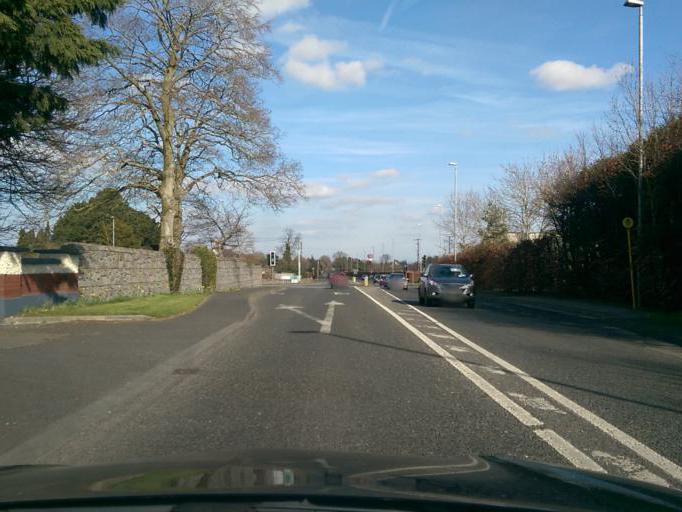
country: IE
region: Leinster
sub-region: Kildare
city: Leixlip
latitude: 53.3440
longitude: -6.5086
